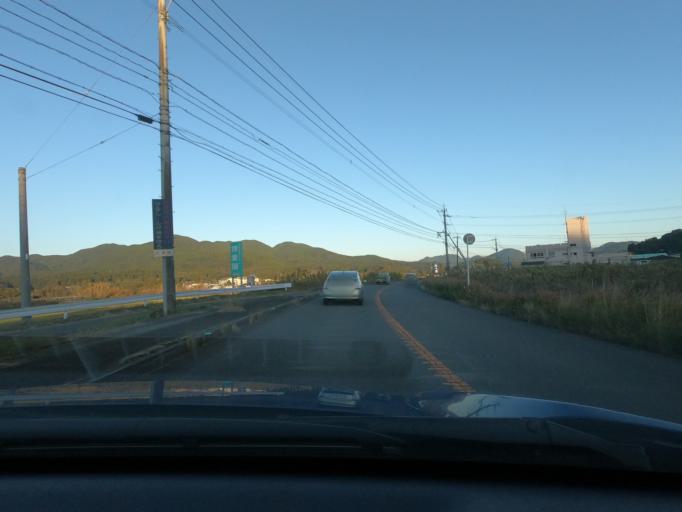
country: JP
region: Kagoshima
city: Satsumasendai
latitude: 31.7990
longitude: 130.4298
